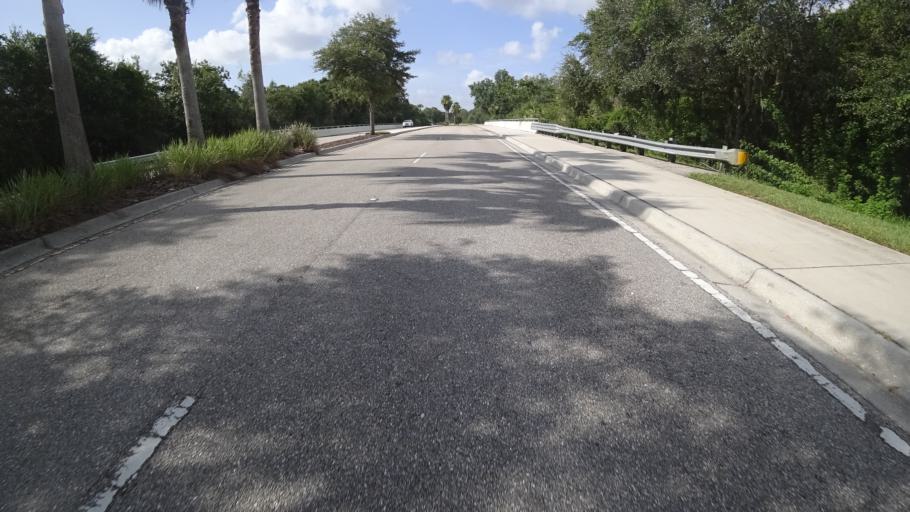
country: US
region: Florida
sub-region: Sarasota County
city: The Meadows
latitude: 27.4071
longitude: -82.4504
